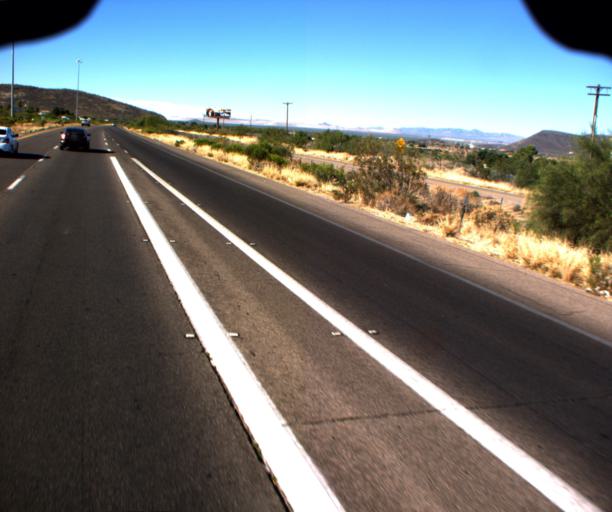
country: US
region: Arizona
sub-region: Pima County
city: Drexel Heights
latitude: 32.1287
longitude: -110.9868
